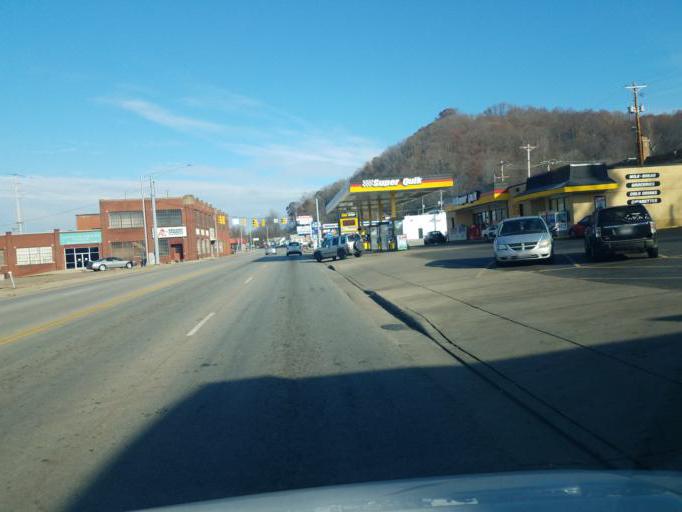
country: US
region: Ohio
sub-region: Scioto County
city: Portsmouth
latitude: 38.7584
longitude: -82.9907
